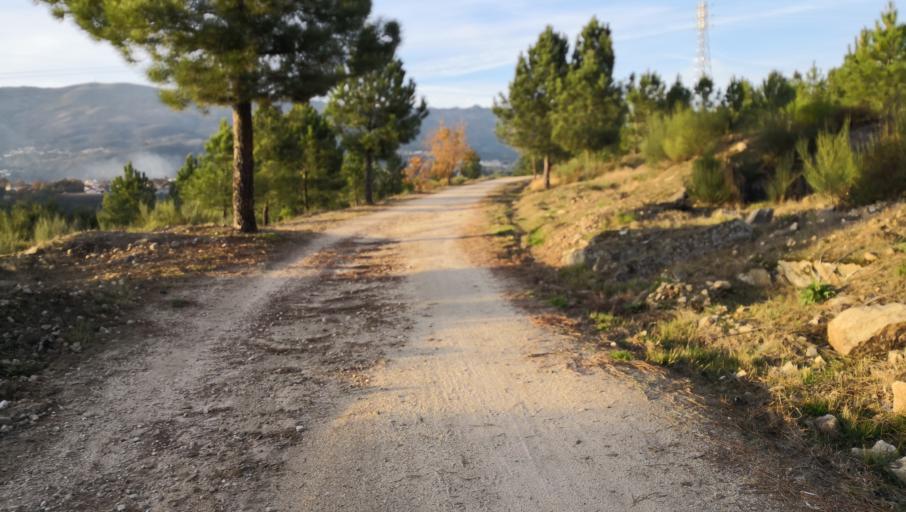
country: PT
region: Vila Real
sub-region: Vila Real
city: Vila Real
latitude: 41.3348
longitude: -7.7091
